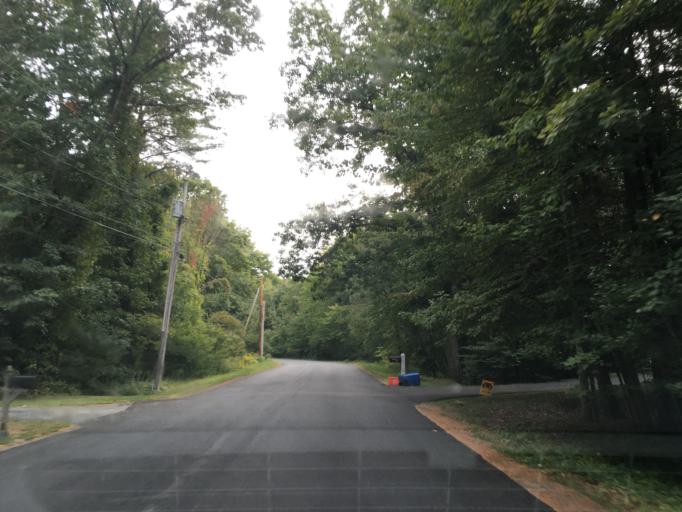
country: US
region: New Hampshire
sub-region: Rockingham County
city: Stratham Station
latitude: 43.0120
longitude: -70.8887
